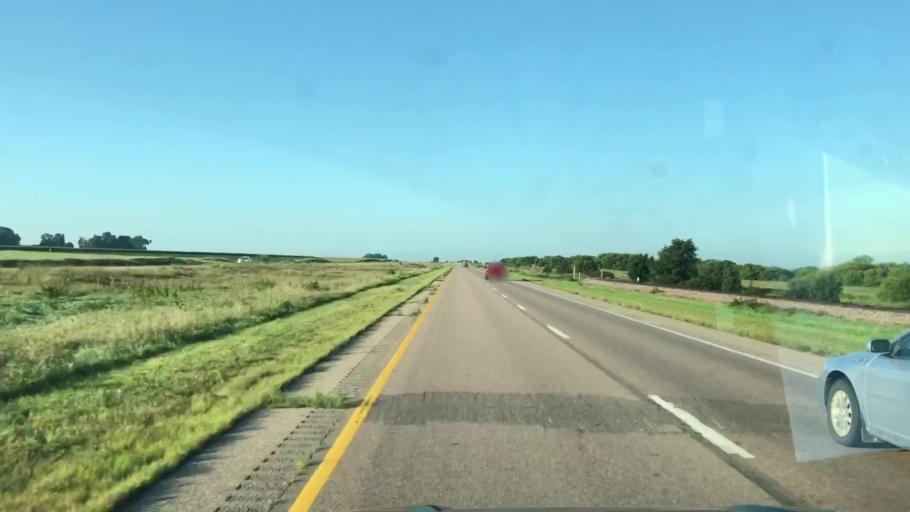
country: US
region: Iowa
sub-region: O'Brien County
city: Sheldon
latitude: 43.1205
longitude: -95.8903
